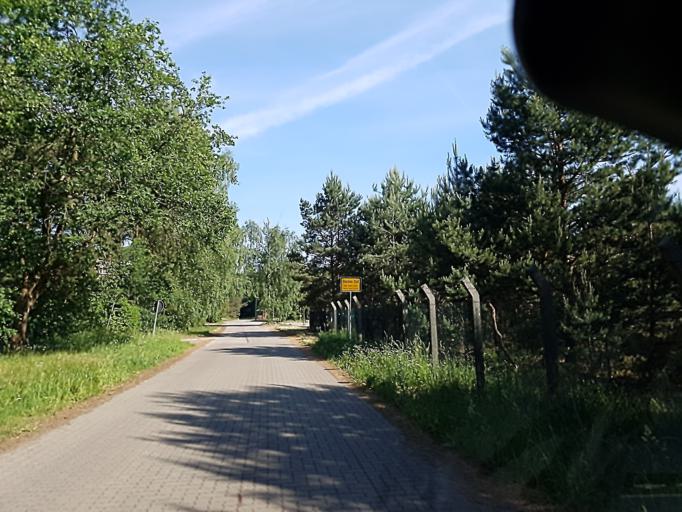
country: DE
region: Brandenburg
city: Gorzke
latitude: 52.0477
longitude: 12.2715
